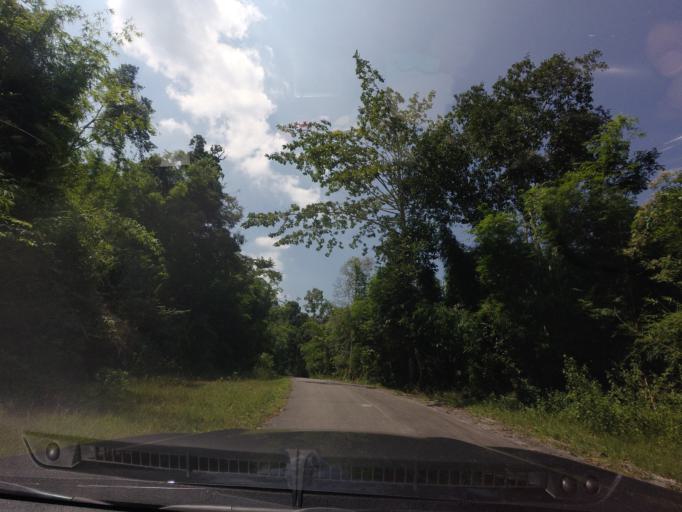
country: TH
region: Loei
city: Na Haeo
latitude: 17.5355
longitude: 100.9407
